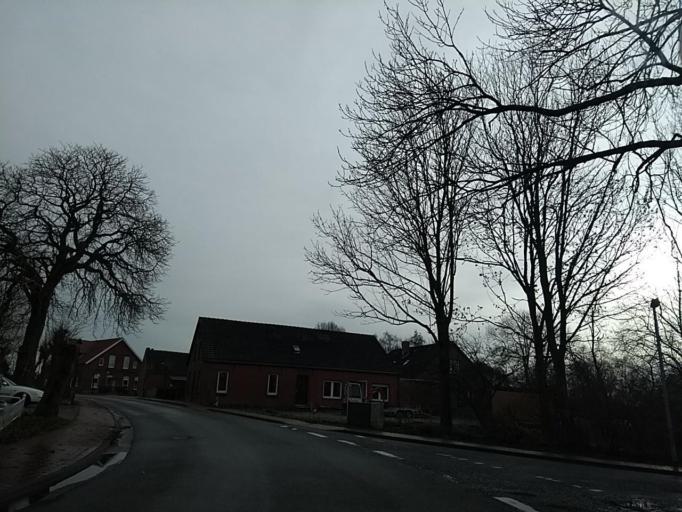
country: DE
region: Lower Saxony
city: Jemgum
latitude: 53.2839
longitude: 7.3718
